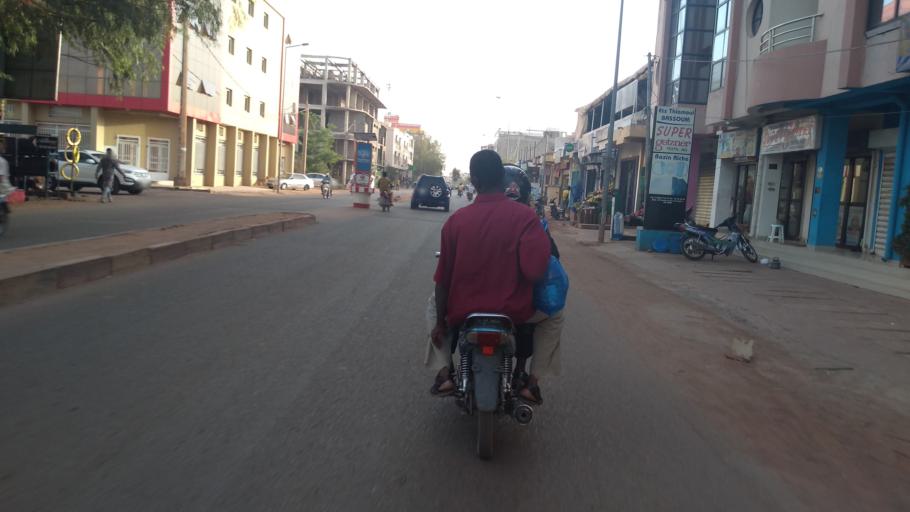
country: ML
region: Bamako
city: Bamako
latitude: 12.6294
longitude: -8.0315
